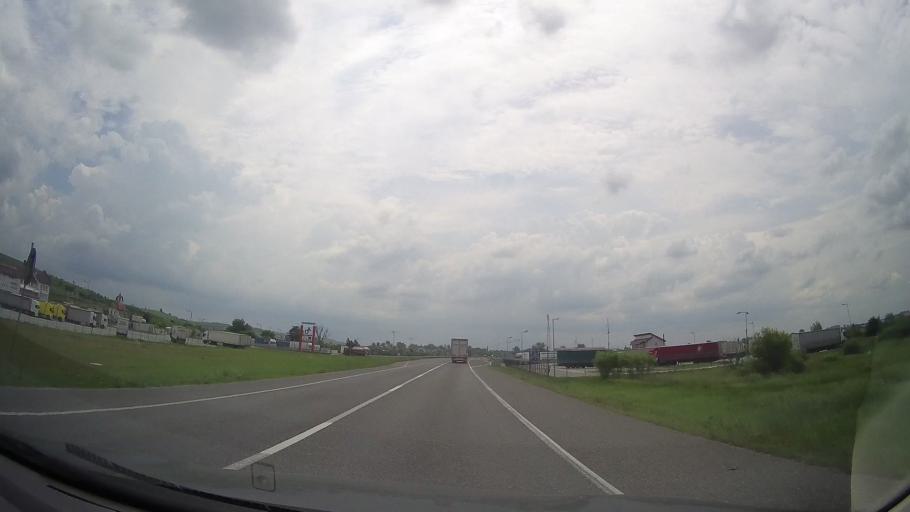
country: RO
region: Timis
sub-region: Municipiul Lugoj
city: Lugoj
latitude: 45.7065
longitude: 21.9175
